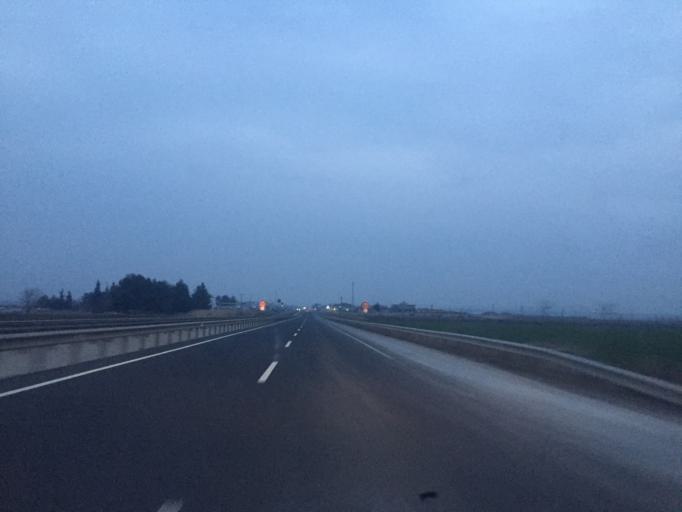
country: TR
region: Sanliurfa
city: Camlidere
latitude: 37.1572
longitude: 39.0450
